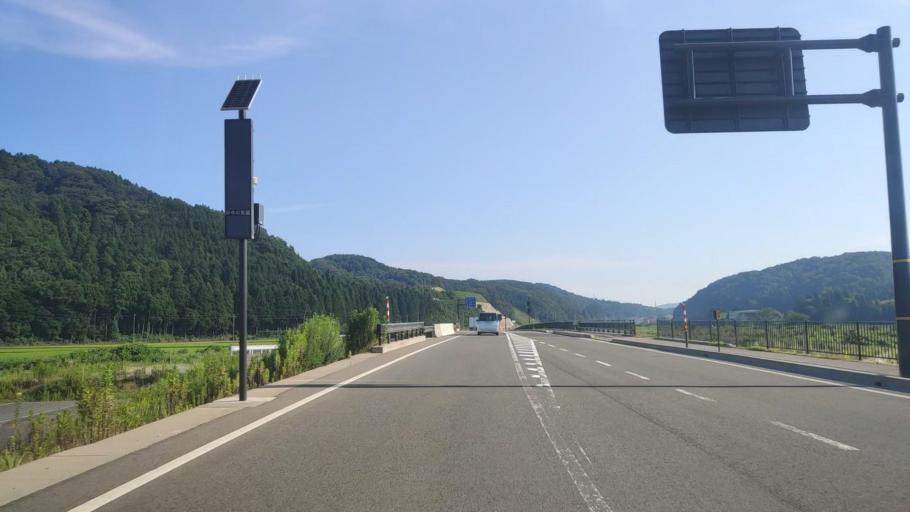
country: JP
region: Fukui
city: Maruoka
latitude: 36.2027
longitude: 136.2676
